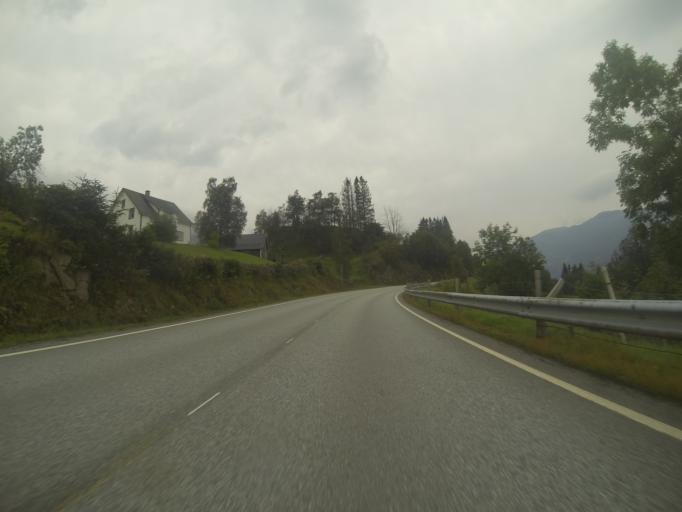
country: NO
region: Rogaland
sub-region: Suldal
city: Sand
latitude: 59.5628
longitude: 6.2706
